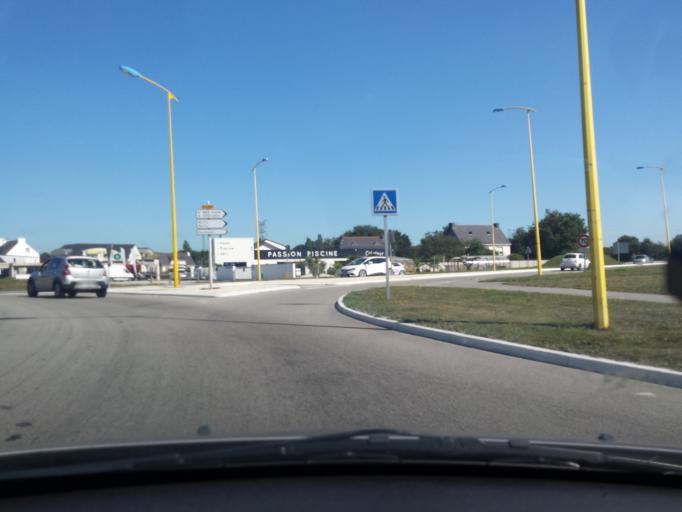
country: FR
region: Brittany
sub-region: Departement du Morbihan
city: Saint-Ave
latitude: 47.6839
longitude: -2.7661
